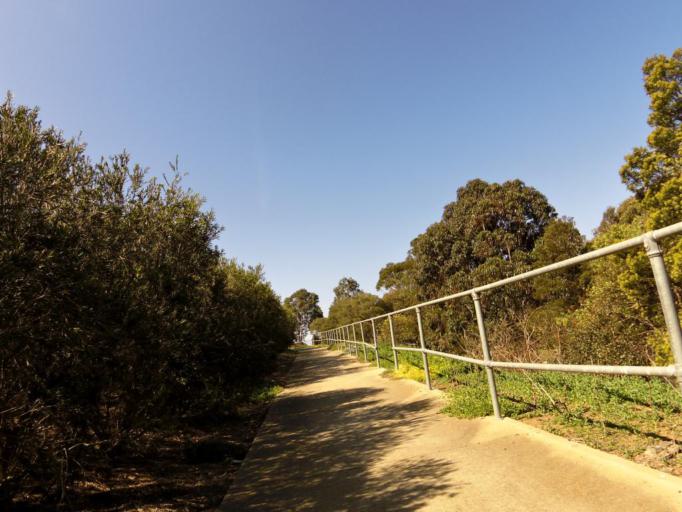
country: AU
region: Victoria
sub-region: Wyndham
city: Werribee
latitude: -37.9200
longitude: 144.6586
